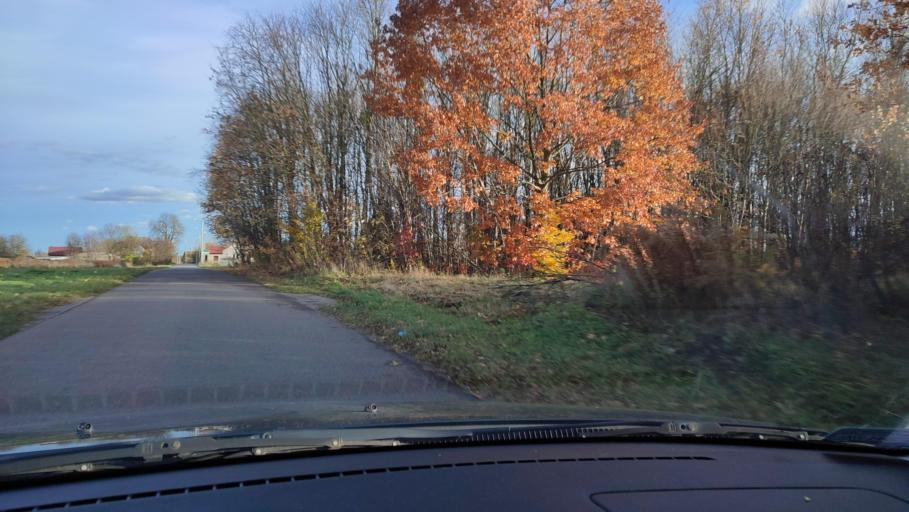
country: PL
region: Warmian-Masurian Voivodeship
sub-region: Powiat szczycienski
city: Szczytno
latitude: 53.5495
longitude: 20.9820
